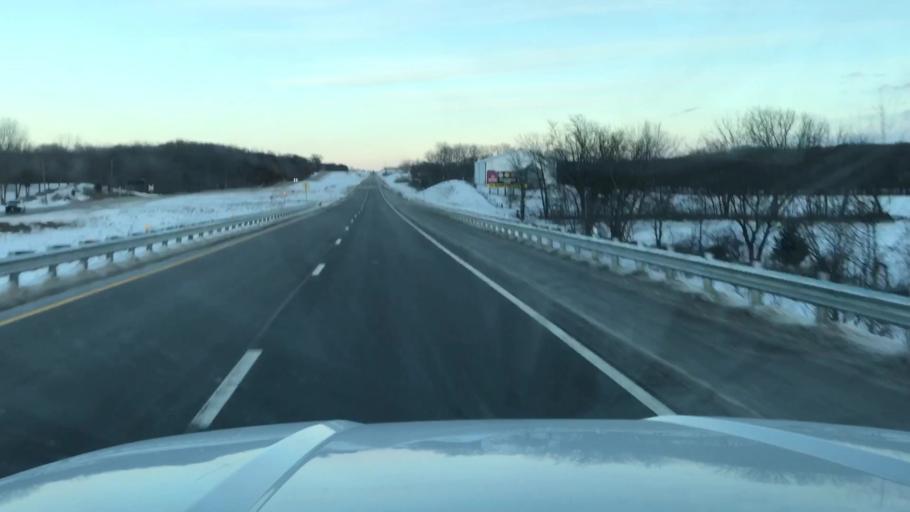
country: US
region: Missouri
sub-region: DeKalb County
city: Maysville
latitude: 39.7620
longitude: -94.4863
